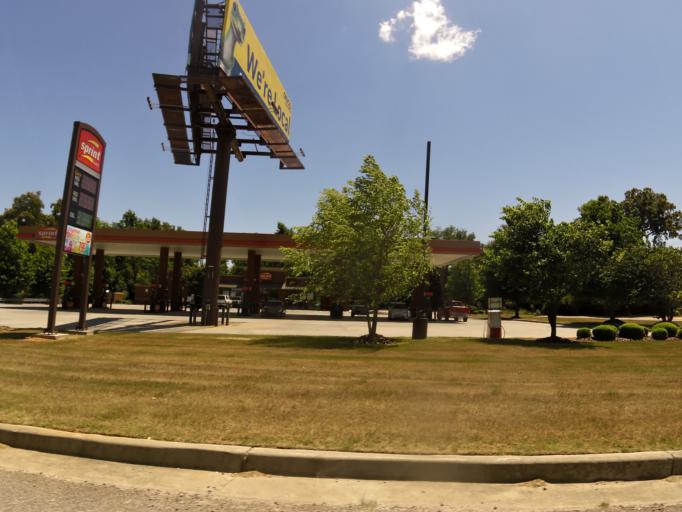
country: US
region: South Carolina
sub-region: Aiken County
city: Clearwater
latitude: 33.4876
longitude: -81.9254
